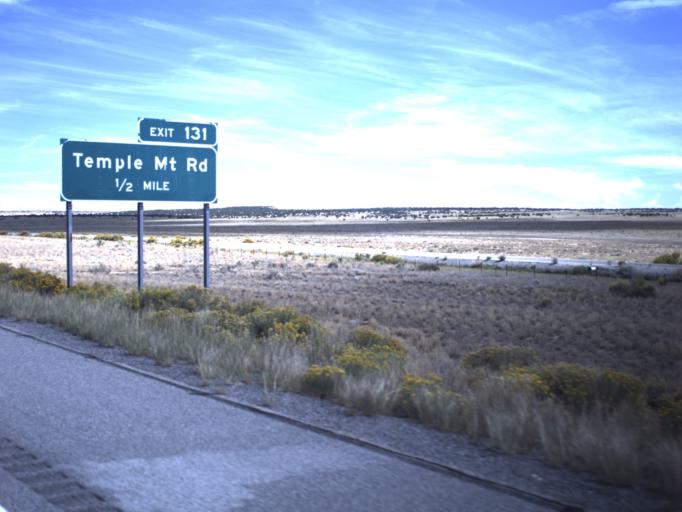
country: US
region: Utah
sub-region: Emery County
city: Castle Dale
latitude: 38.8755
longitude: -110.6700
